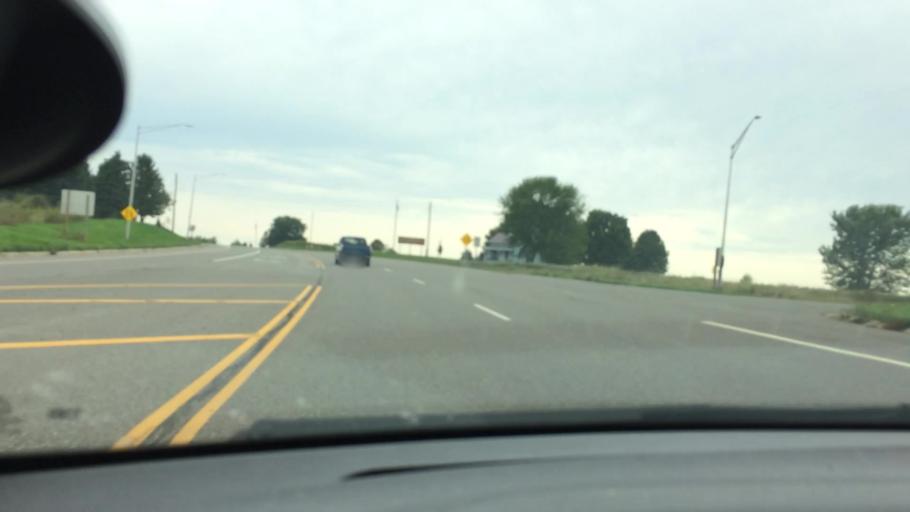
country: US
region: Wisconsin
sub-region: Clark County
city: Neillsville
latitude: 44.5590
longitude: -90.6431
